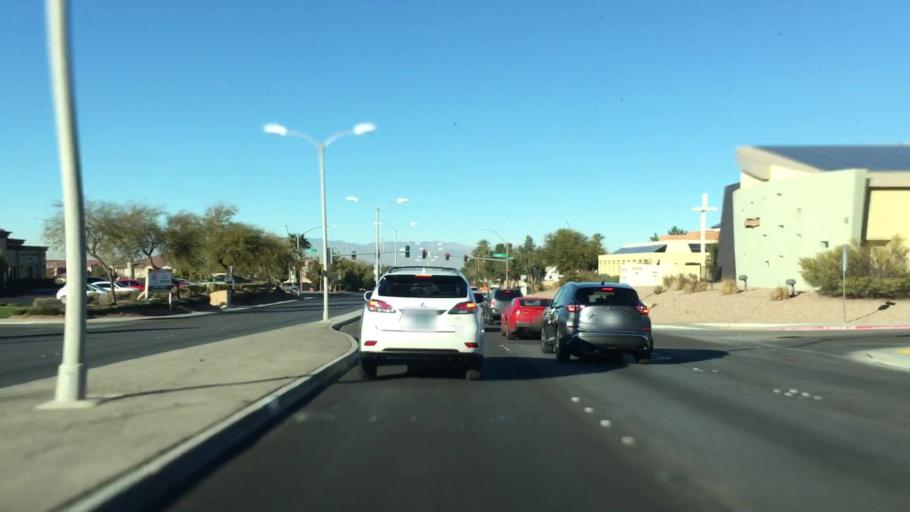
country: US
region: Nevada
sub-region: Clark County
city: Whitney
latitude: 36.0264
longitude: -115.1005
